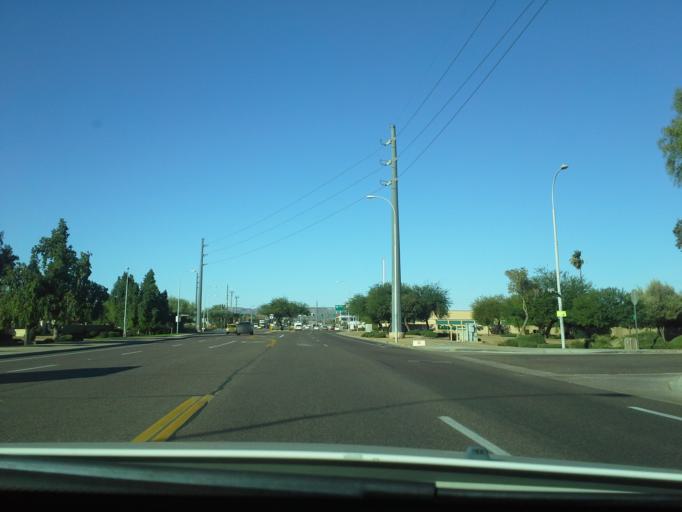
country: US
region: Arizona
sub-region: Maricopa County
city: San Carlos
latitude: 33.3494
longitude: -111.8899
